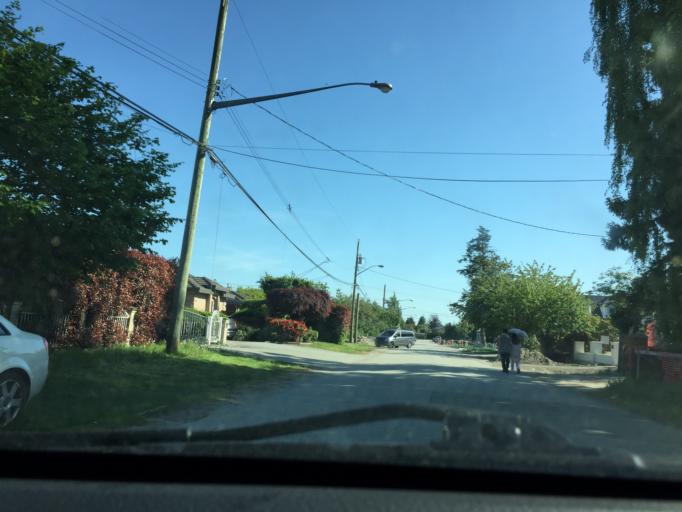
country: CA
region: British Columbia
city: Richmond
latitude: 49.1580
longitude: -123.1170
